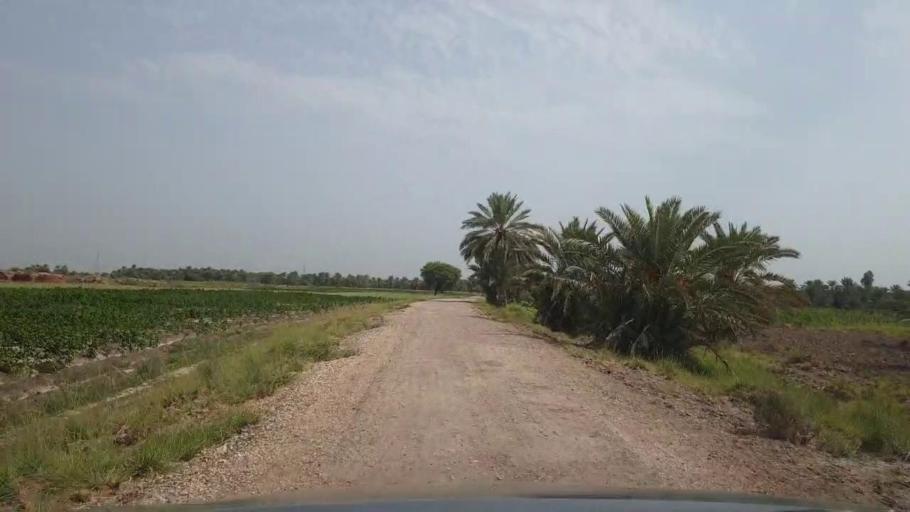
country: PK
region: Sindh
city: Rohri
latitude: 27.6822
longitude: 69.0358
